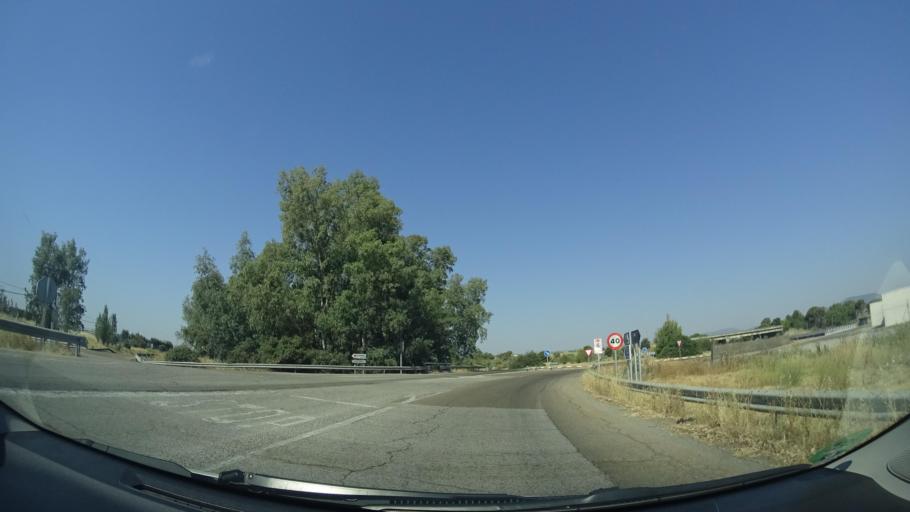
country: ES
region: Extremadura
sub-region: Provincia de Caceres
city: Miajadas
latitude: 39.1346
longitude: -5.9424
